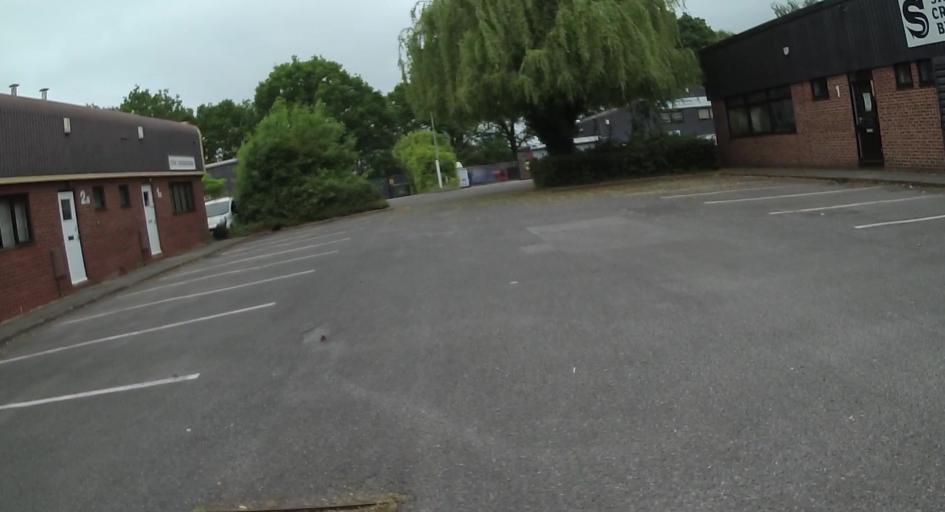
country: GB
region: England
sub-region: Hampshire
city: Eversley
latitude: 51.3765
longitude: -0.8926
